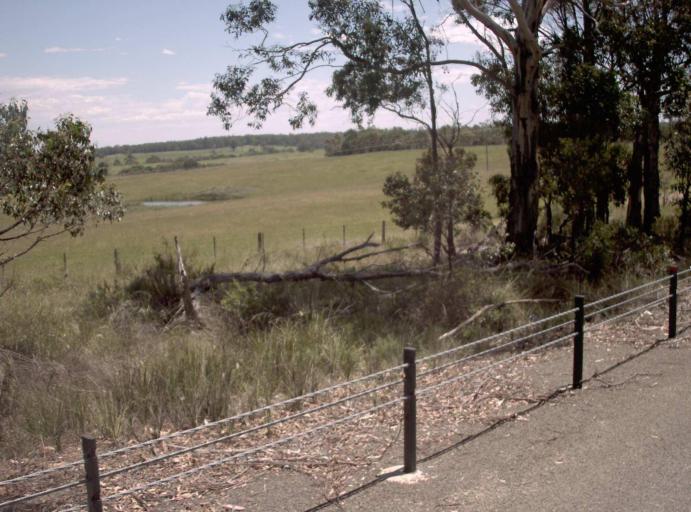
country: AU
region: Victoria
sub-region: East Gippsland
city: Lakes Entrance
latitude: -37.8369
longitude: 148.0323
